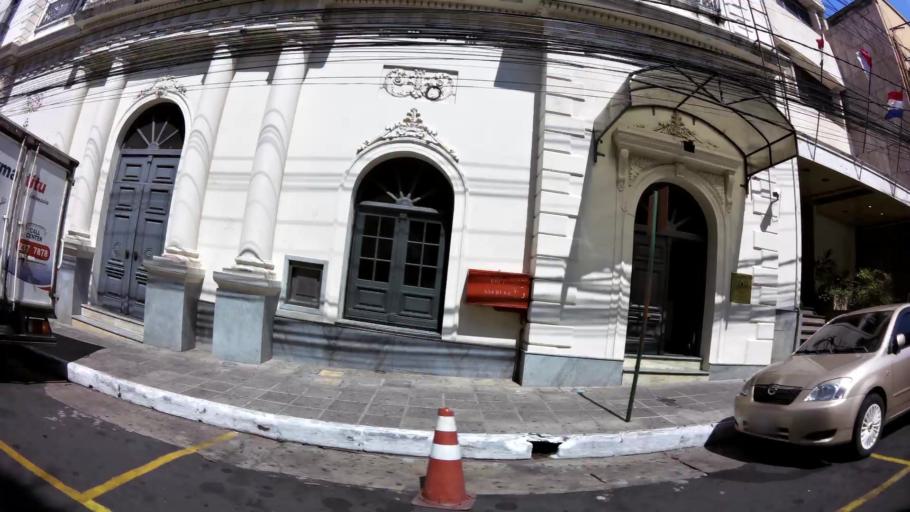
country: PY
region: Asuncion
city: Asuncion
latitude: -25.2813
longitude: -57.6369
